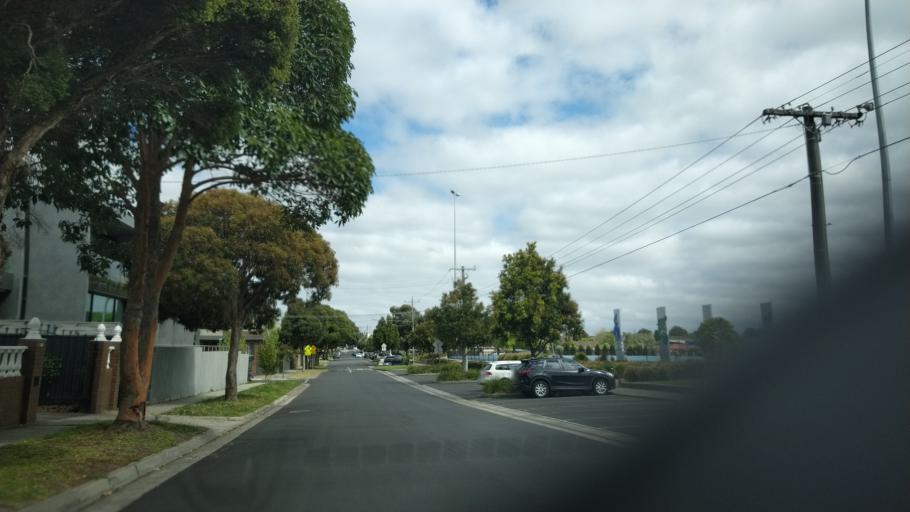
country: AU
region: Victoria
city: Murrumbeena
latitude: -37.9023
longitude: 145.0589
